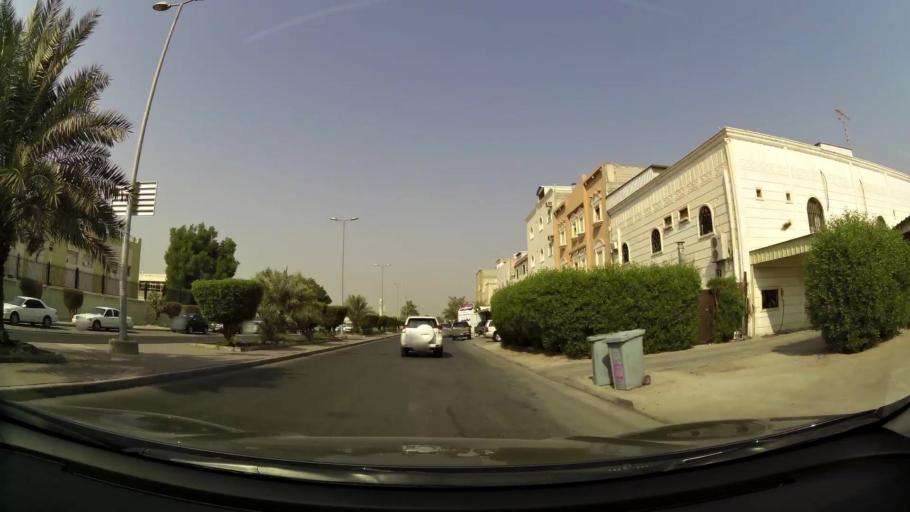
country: KW
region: Al Asimah
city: Ar Rabiyah
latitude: 29.2818
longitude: 47.8779
